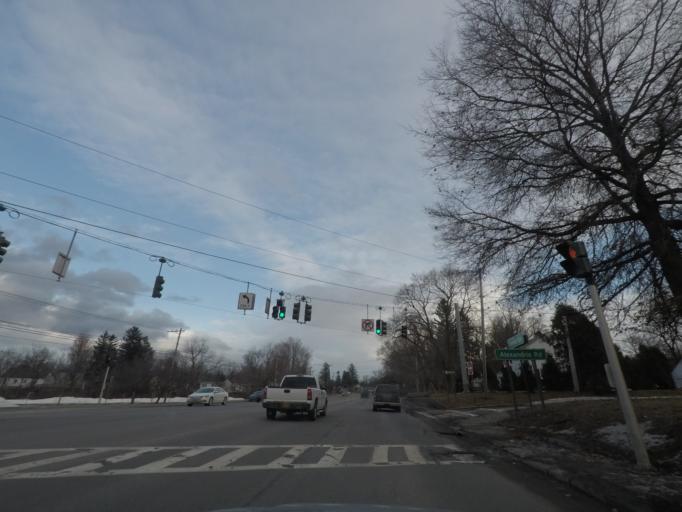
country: US
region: New York
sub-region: Oneida County
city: New Hartford
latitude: 43.0787
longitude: -75.3151
